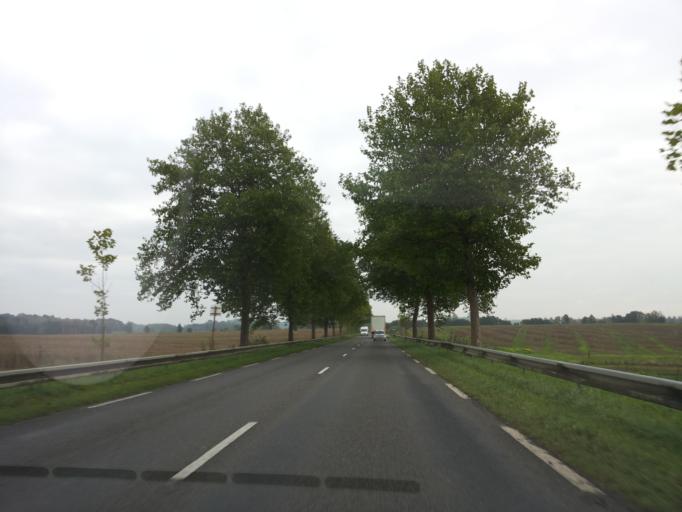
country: FR
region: Champagne-Ardenne
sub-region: Departement des Ardennes
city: Pouru-Saint-Remy
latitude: 49.6745
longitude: 5.1041
